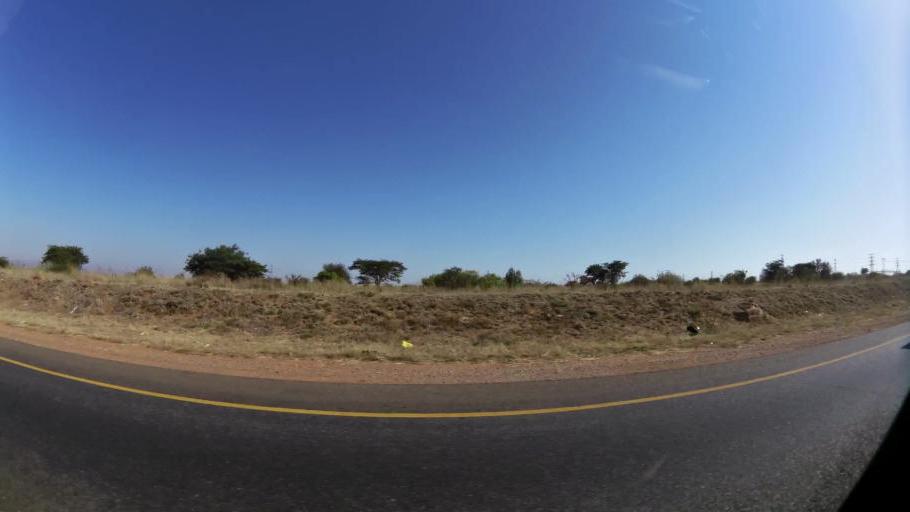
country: ZA
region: Gauteng
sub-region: City of Tshwane Metropolitan Municipality
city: Mabopane
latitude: -25.5678
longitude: 28.1076
